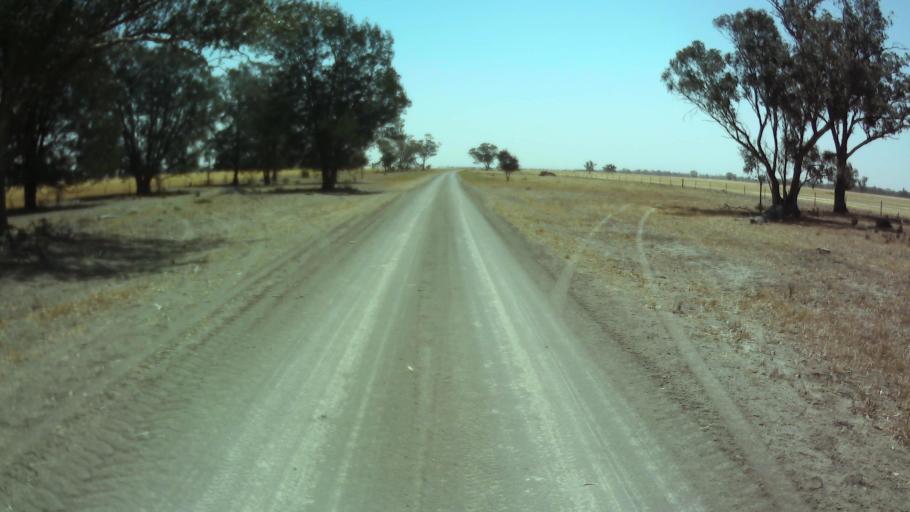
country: AU
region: New South Wales
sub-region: Weddin
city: Grenfell
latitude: -33.9967
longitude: 147.8757
